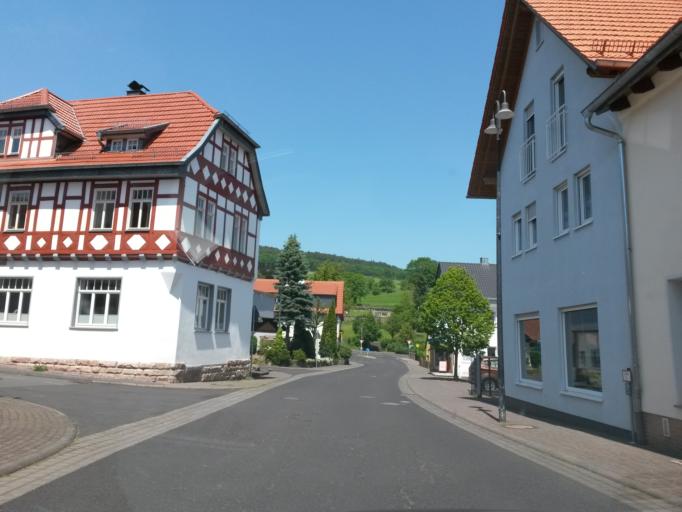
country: DE
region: Thuringia
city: Birx
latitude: 50.5016
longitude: 10.0046
